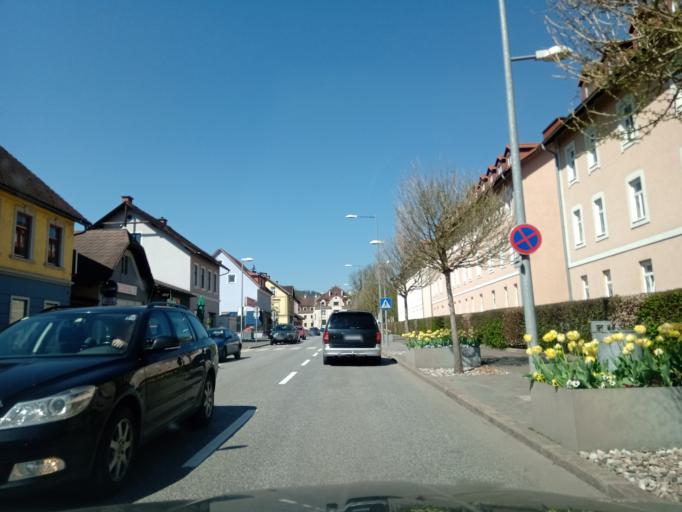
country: AT
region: Styria
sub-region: Politischer Bezirk Leoben
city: Leoben
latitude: 47.3758
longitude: 15.0767
